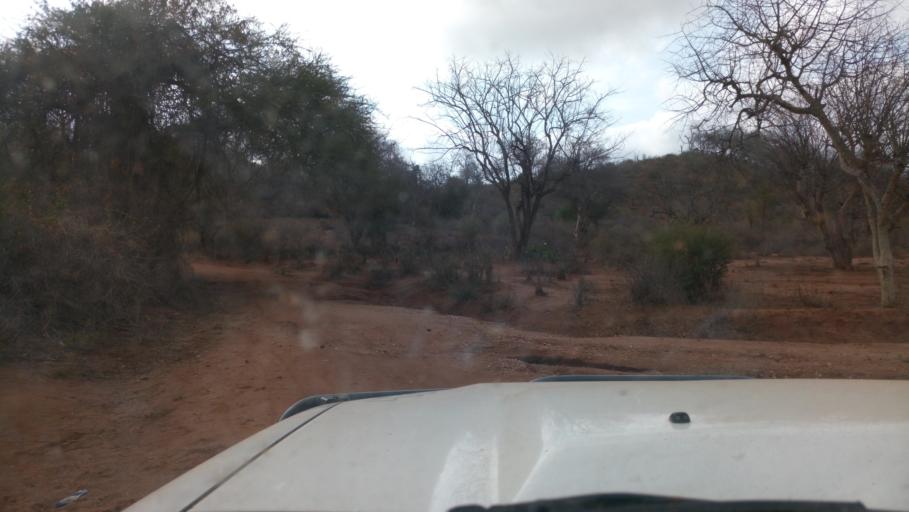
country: KE
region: Kitui
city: Kitui
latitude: -1.8586
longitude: 38.2902
